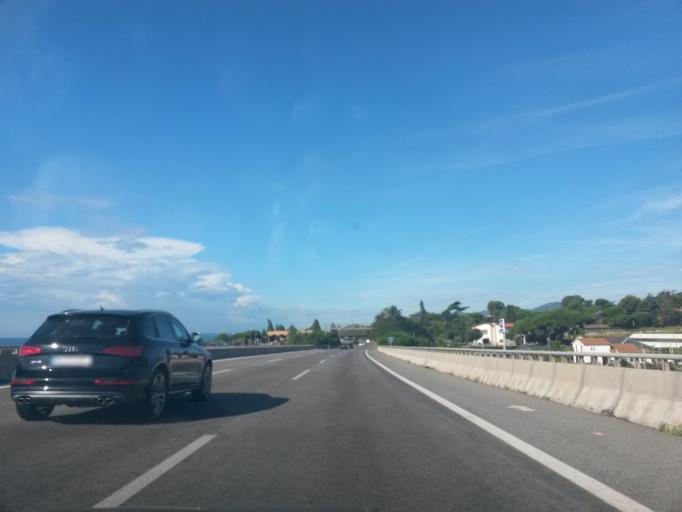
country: ES
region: Catalonia
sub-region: Provincia de Barcelona
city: Sant Andreu de Llavaneres
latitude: 41.5642
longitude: 2.4938
